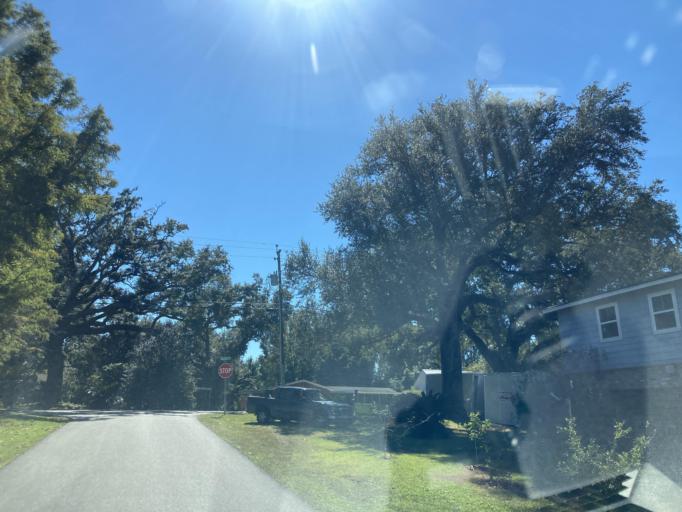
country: US
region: Mississippi
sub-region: Jackson County
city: Ocean Springs
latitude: 30.4080
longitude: -88.8199
